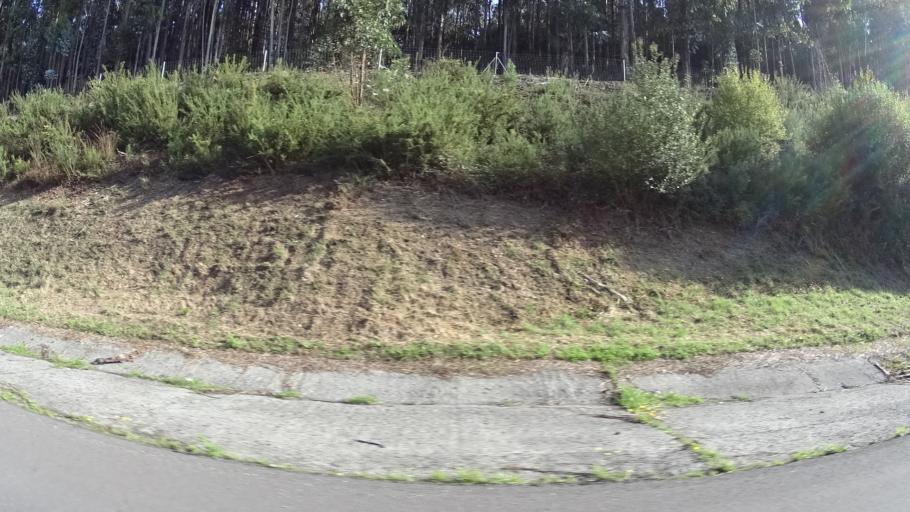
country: ES
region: Galicia
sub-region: Provincia da Coruna
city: Coiros
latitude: 43.2416
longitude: -8.1675
